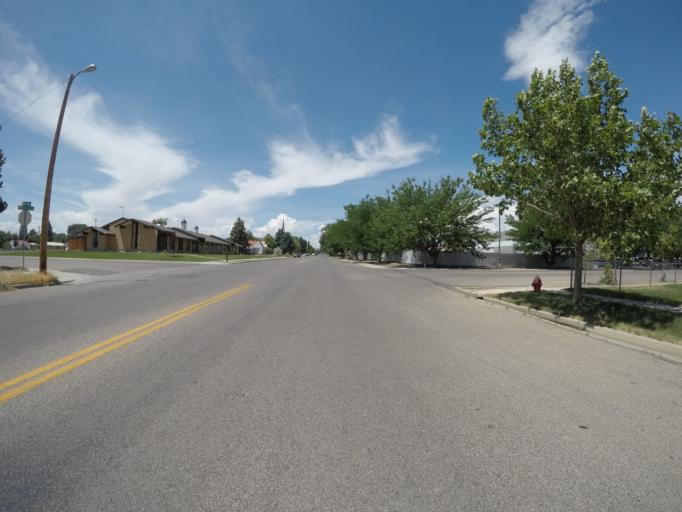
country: US
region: Utah
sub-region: Uintah County
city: Vernal
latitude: 40.4543
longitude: -109.5346
